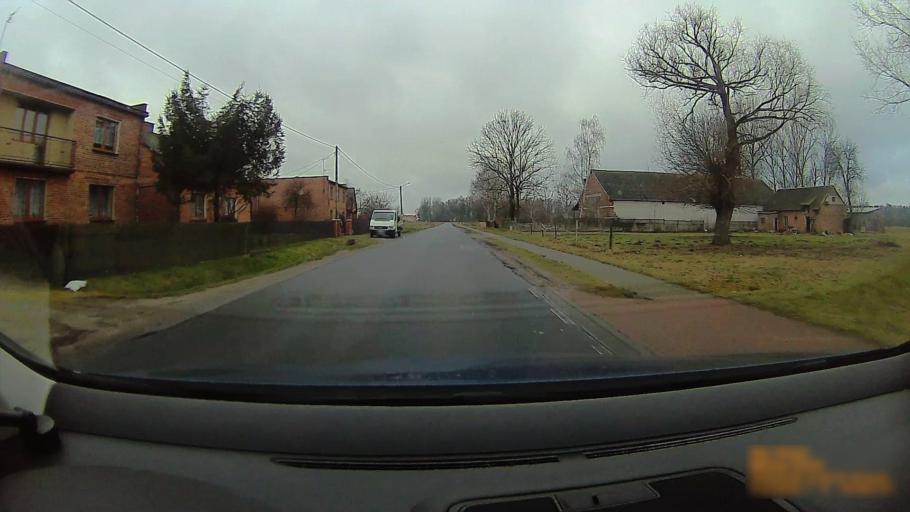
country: PL
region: Greater Poland Voivodeship
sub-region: Powiat koninski
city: Rychwal
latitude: 52.0960
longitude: 18.1510
